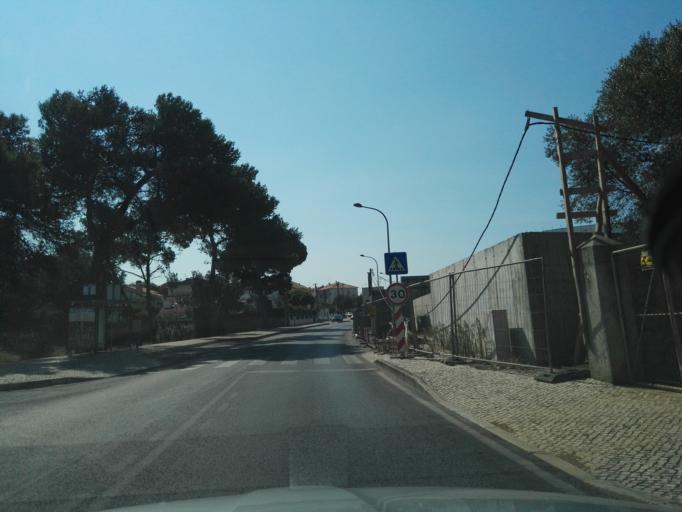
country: PT
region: Lisbon
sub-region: Cascais
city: Estoril
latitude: 38.7112
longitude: -9.3863
